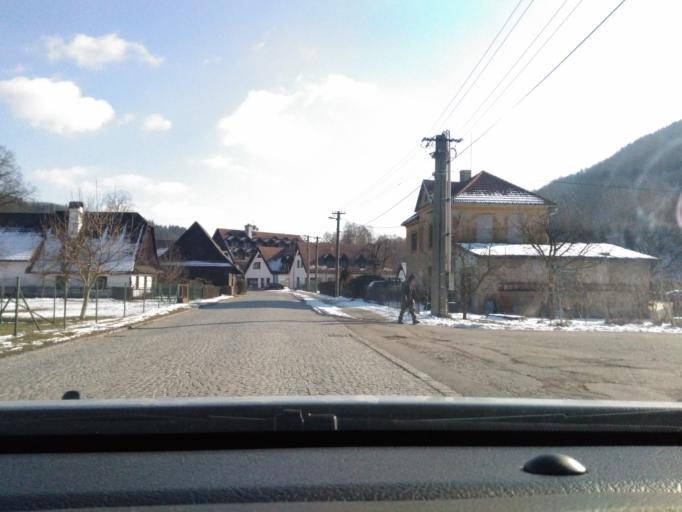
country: CZ
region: Vysocina
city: Bystrice nad Pernstejnem
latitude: 49.5559
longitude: 16.3272
